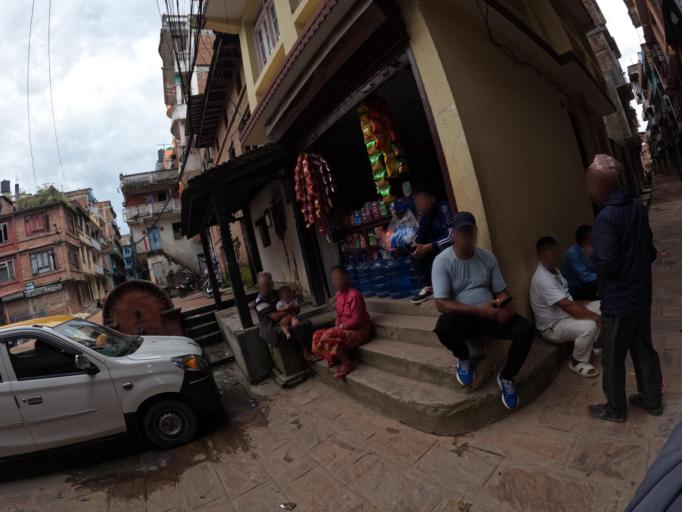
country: NP
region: Central Region
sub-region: Bagmati Zone
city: Kathmandu
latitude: 27.7675
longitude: 85.3296
